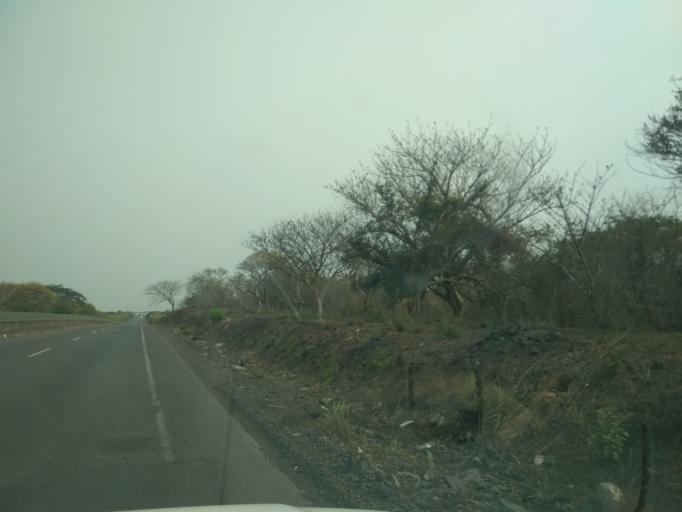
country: MX
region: Veracruz
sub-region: Veracruz
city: Las Amapolas
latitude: 19.1339
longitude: -96.2508
